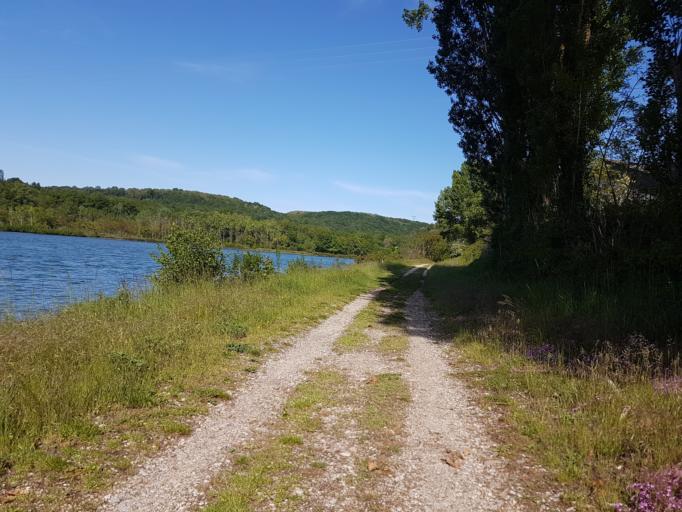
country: FR
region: Rhone-Alpes
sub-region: Departement de l'Ain
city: Villebois
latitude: 45.8395
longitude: 5.4215
